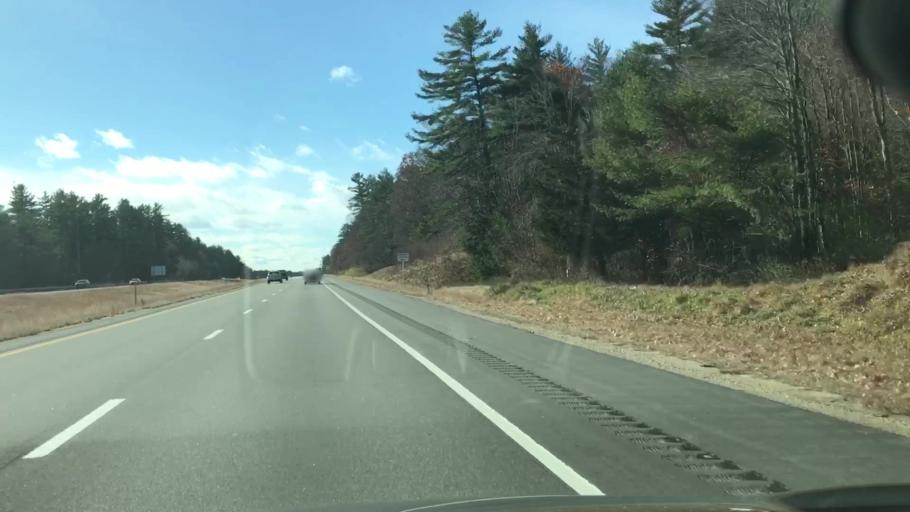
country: US
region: New Hampshire
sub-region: Merrimack County
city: East Concord
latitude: 43.2343
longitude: -71.4809
